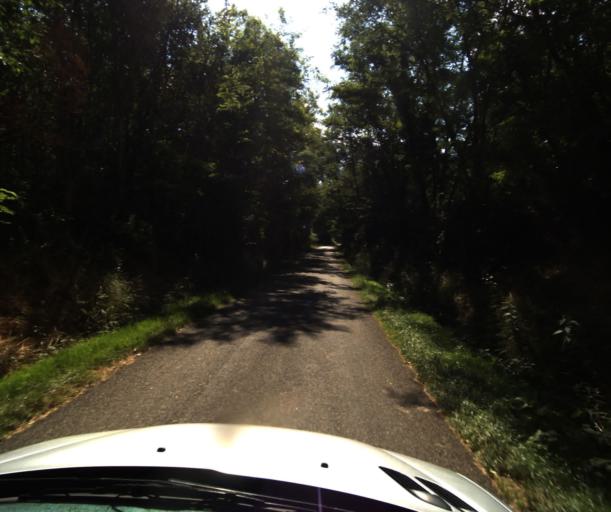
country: FR
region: Midi-Pyrenees
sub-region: Departement du Tarn-et-Garonne
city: Finhan
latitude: 43.9002
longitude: 1.2688
